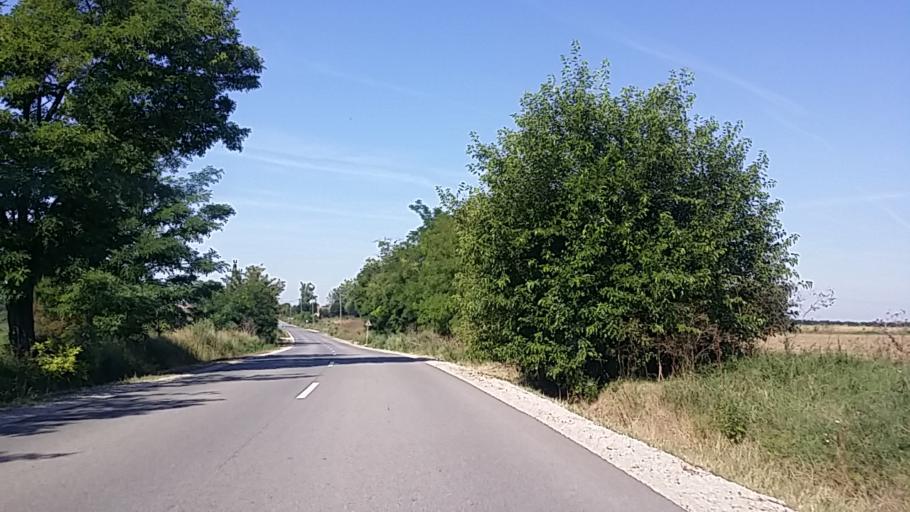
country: HU
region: Fejer
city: Pusztaszabolcs
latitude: 47.1178
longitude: 18.7833
